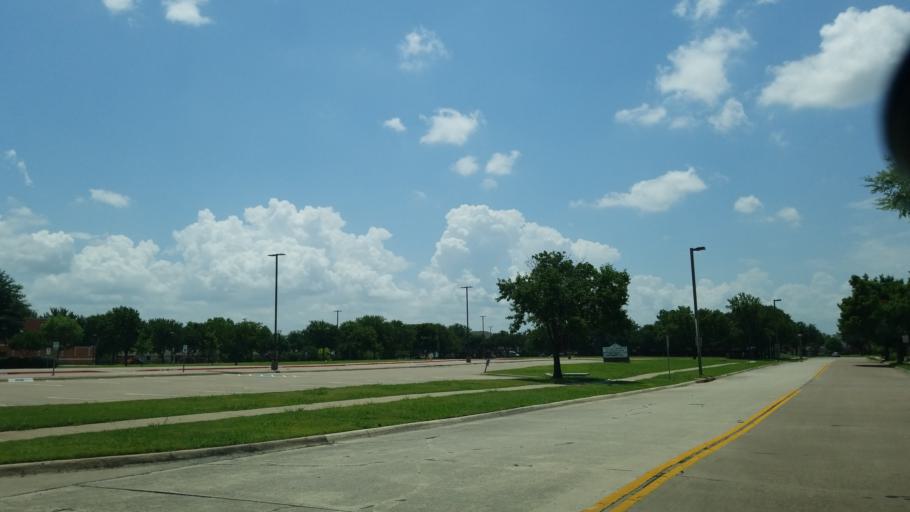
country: US
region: Texas
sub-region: Dallas County
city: Coppell
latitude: 32.9379
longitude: -96.9570
